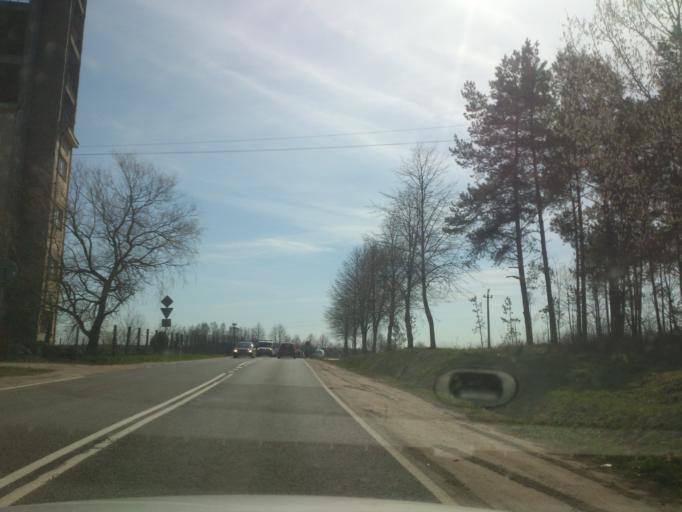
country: PL
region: Masovian Voivodeship
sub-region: Powiat mlawski
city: Szydlowo
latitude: 53.0953
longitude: 20.4176
